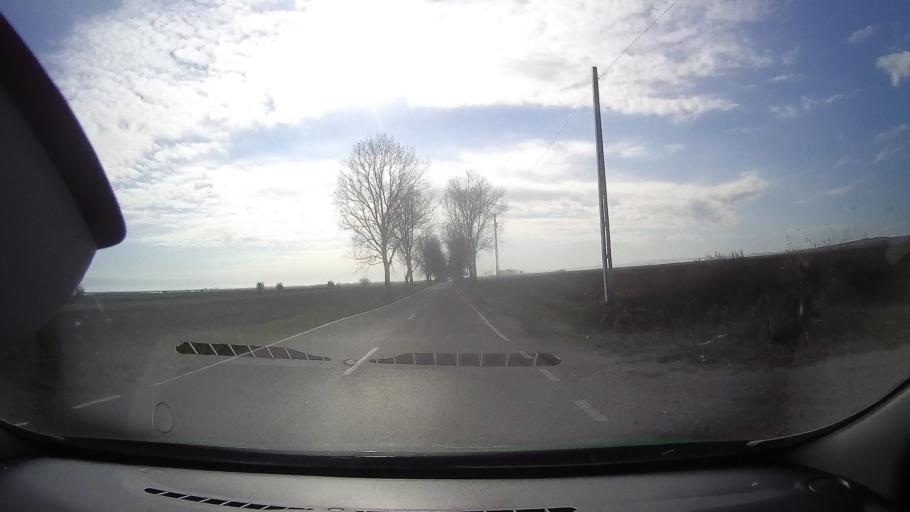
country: RO
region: Tulcea
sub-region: Comuna Valea Nucarilor
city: Agighiol
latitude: 45.0080
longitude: 28.8848
